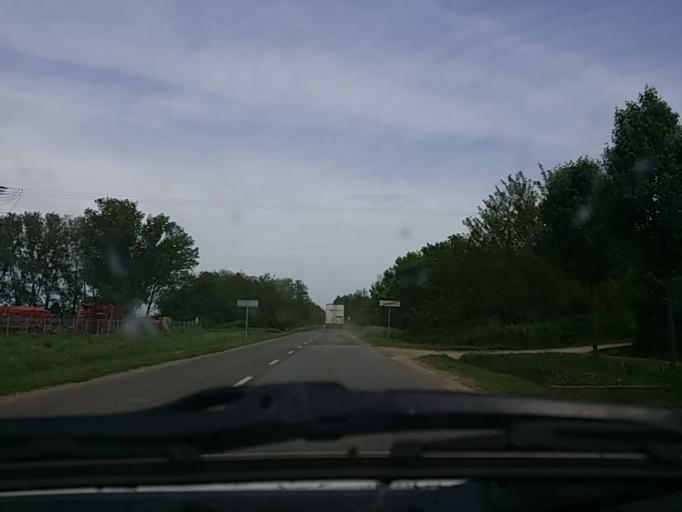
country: HU
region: Baranya
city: Vajszlo
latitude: 45.8803
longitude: 17.9192
